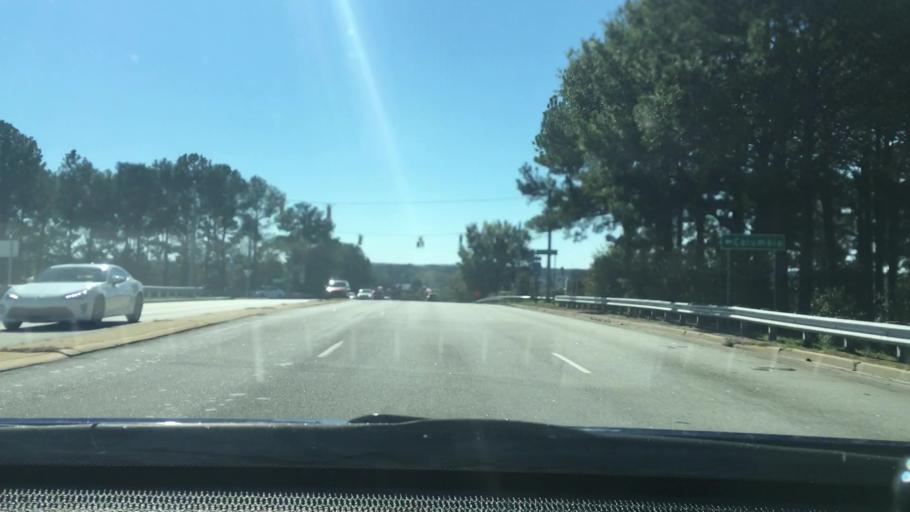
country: US
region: South Carolina
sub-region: Lexington County
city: Seven Oaks
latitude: 34.0776
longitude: -81.1530
